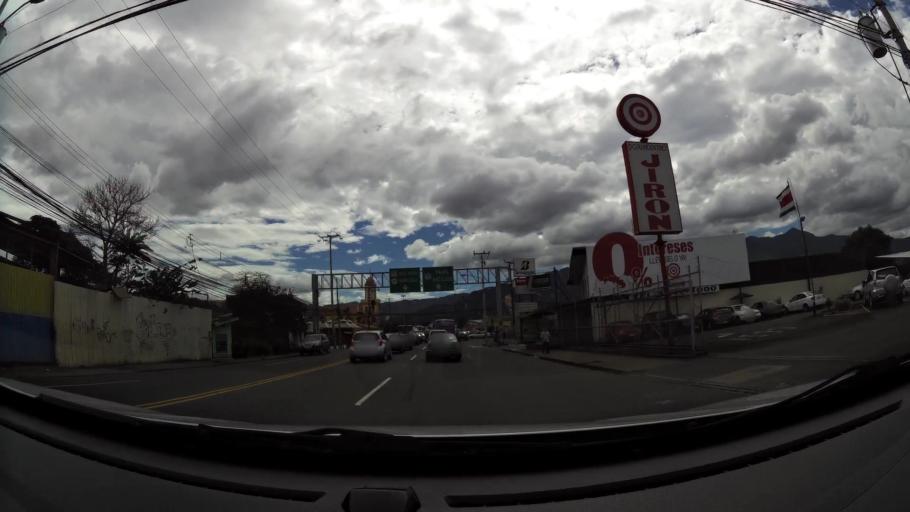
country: CR
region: San Jose
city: Alajuelita
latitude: 9.9122
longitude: -84.0851
